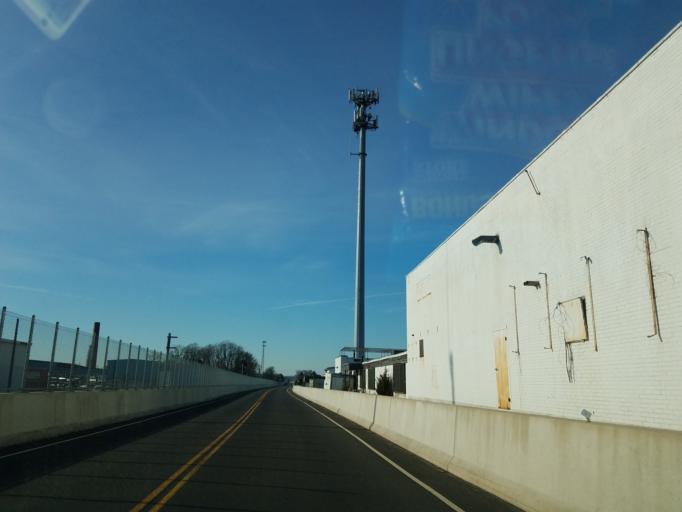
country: US
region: Connecticut
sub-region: Hartford County
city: West Hartford
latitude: 41.7368
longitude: -72.7200
